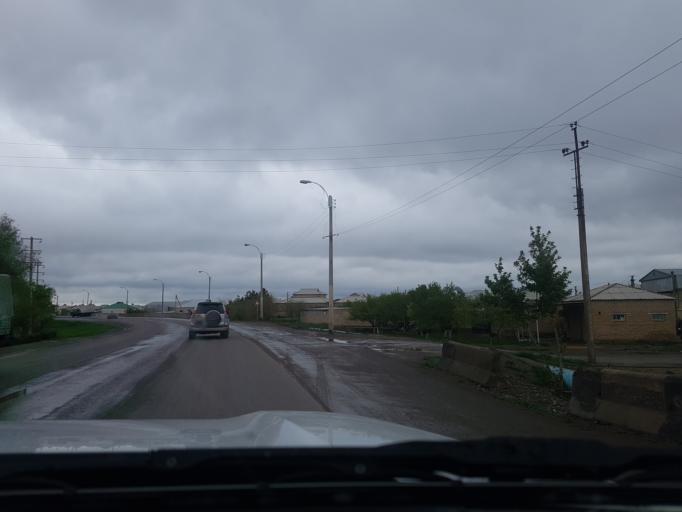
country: TM
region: Mary
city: Mary
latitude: 37.5852
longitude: 61.8802
